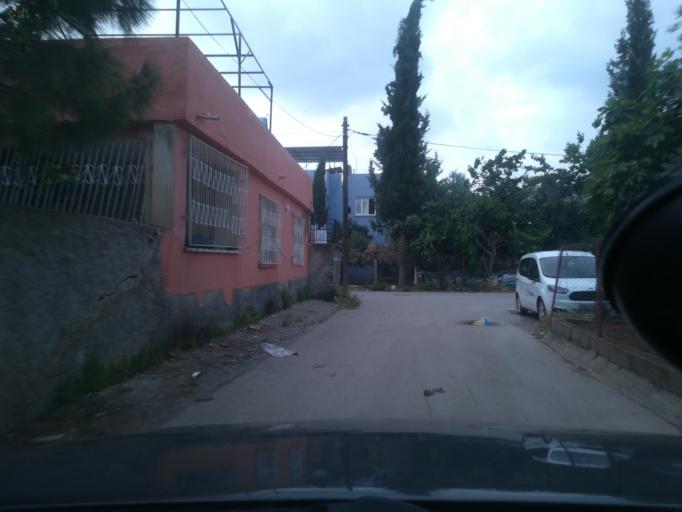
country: TR
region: Adana
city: Seyhan
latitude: 37.0148
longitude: 35.2710
